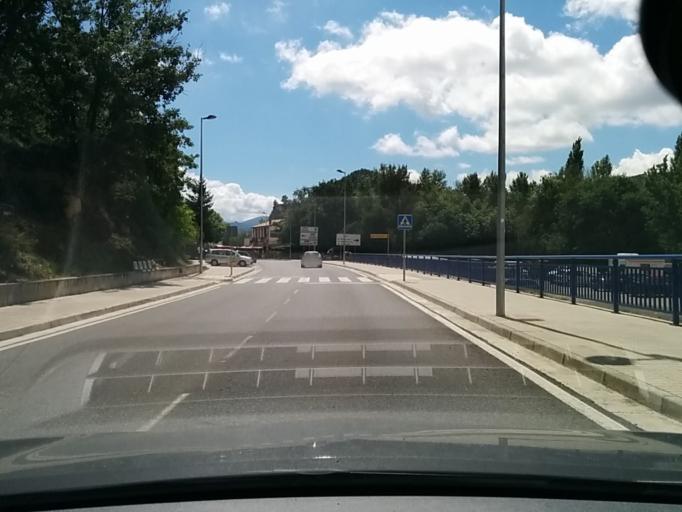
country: ES
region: Aragon
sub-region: Provincia de Huesca
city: Ainsa
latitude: 42.4157
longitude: 0.1379
